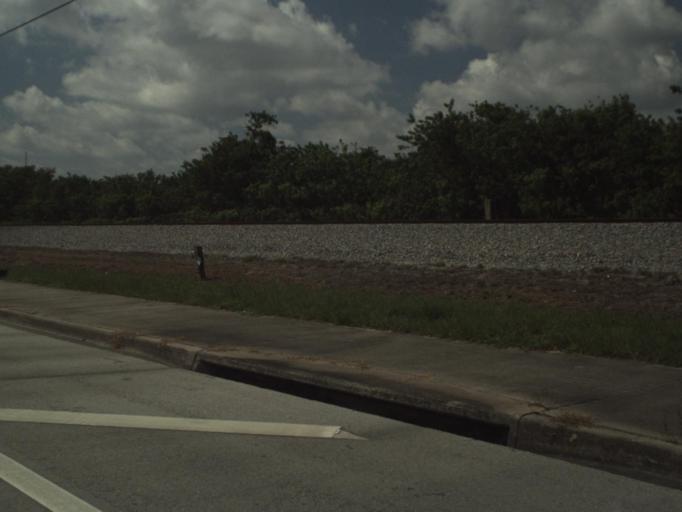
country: US
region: Florida
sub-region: Palm Beach County
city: North Palm Beach
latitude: 26.8186
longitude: -80.0829
